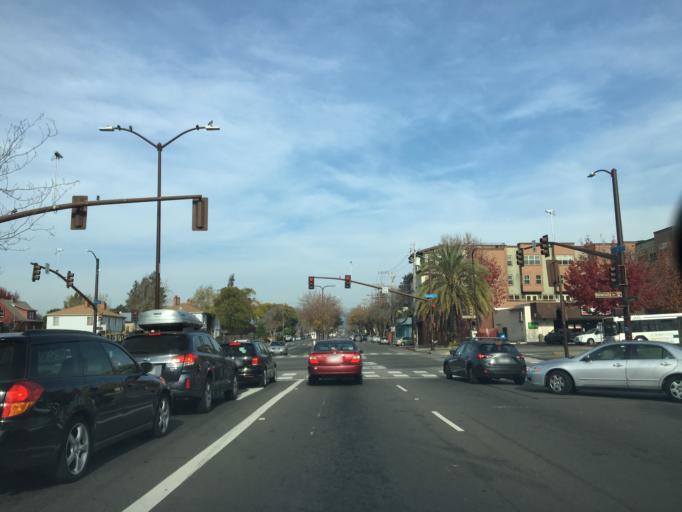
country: US
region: California
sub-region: Alameda County
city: Berkeley
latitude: 37.8700
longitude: -122.2819
